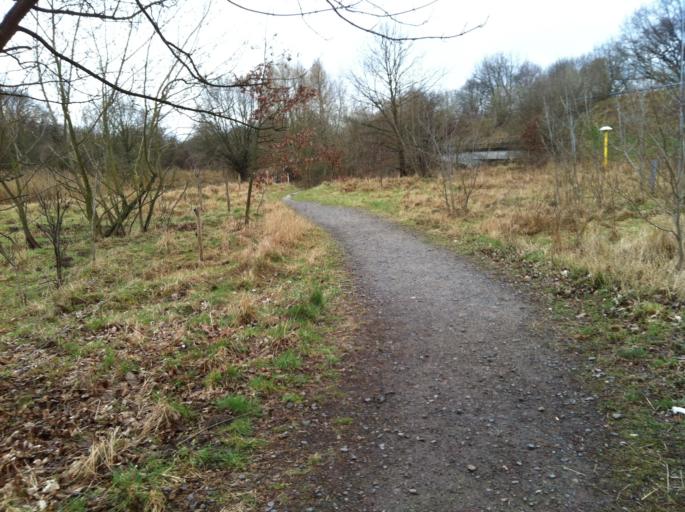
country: DE
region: Berlin
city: Karow
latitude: 52.6291
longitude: 13.4644
